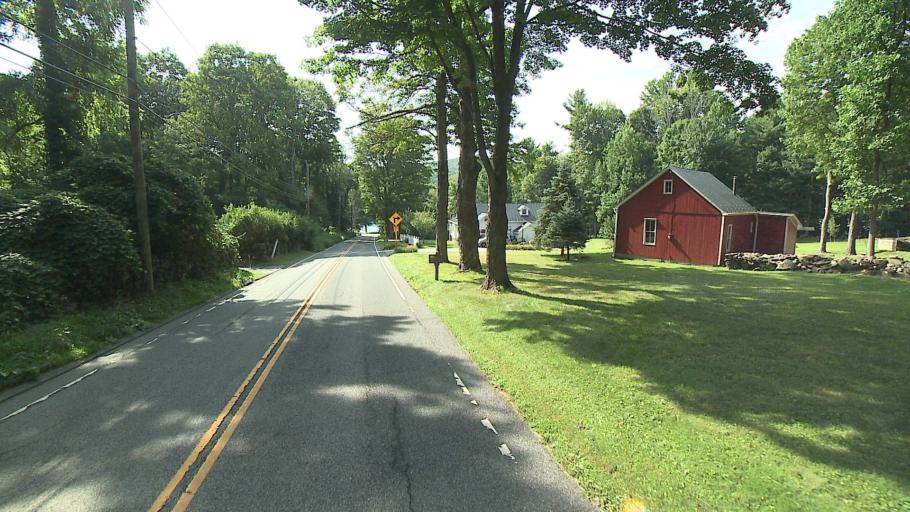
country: US
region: Connecticut
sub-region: Fairfield County
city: Sherman
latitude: 41.5432
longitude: -73.4992
